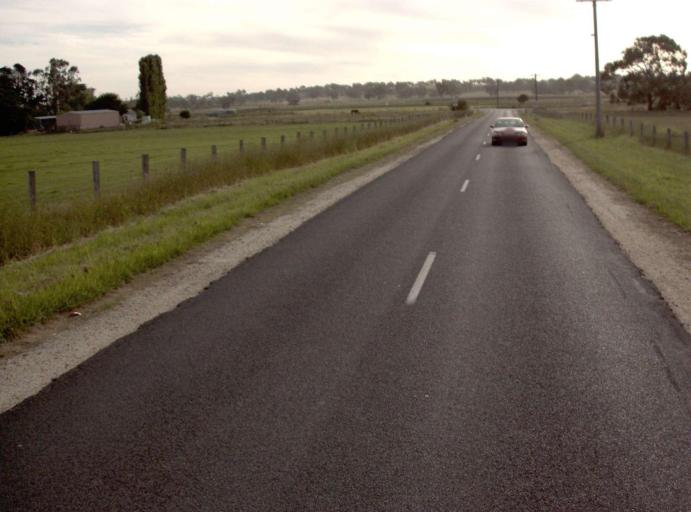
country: AU
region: Victoria
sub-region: Wellington
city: Heyfield
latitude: -37.8791
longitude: 146.9900
